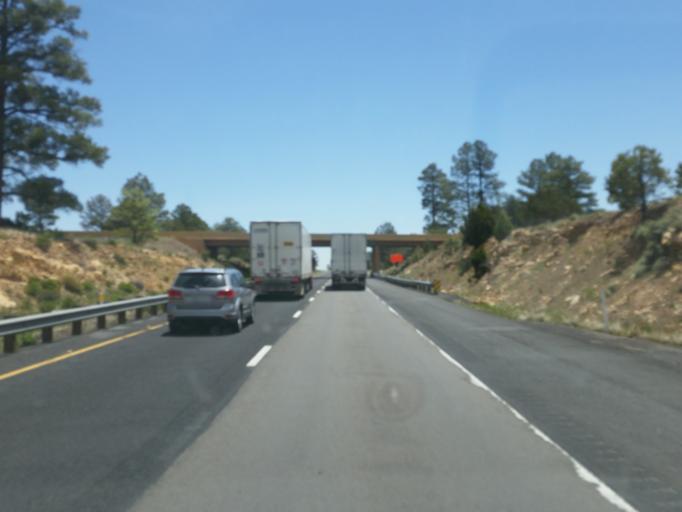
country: US
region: Arizona
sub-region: Coconino County
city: Flagstaff
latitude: 35.2087
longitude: -111.5184
